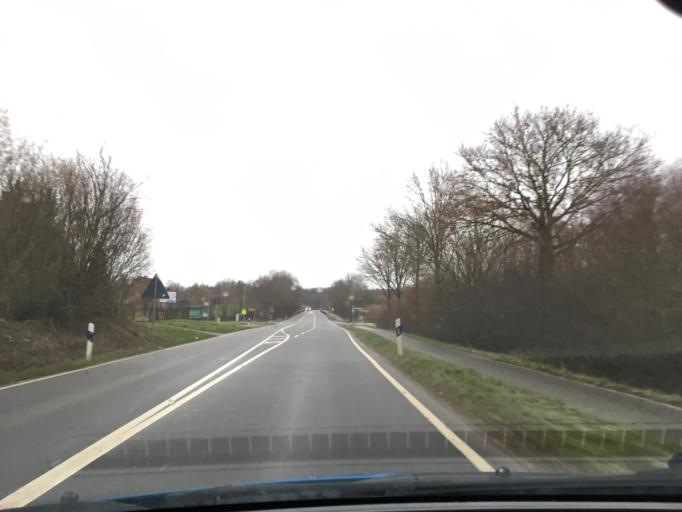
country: DE
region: Schleswig-Holstein
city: Hornbek
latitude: 53.5578
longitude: 10.6488
